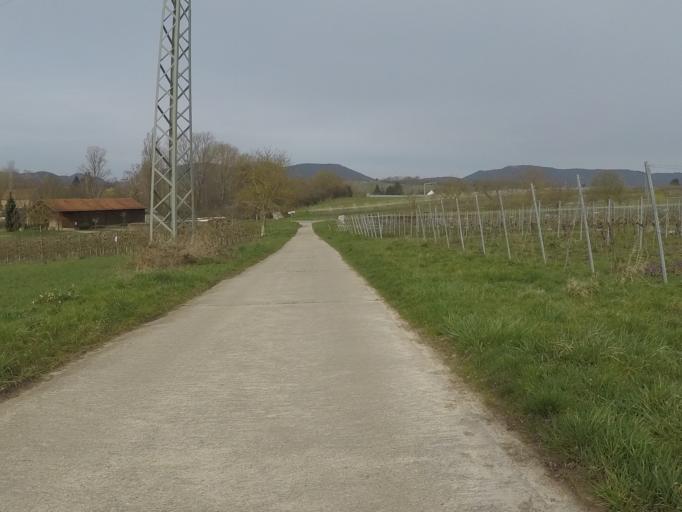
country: DE
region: Rheinland-Pfalz
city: Heuchelheim-Klingen
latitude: 49.1410
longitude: 8.0637
